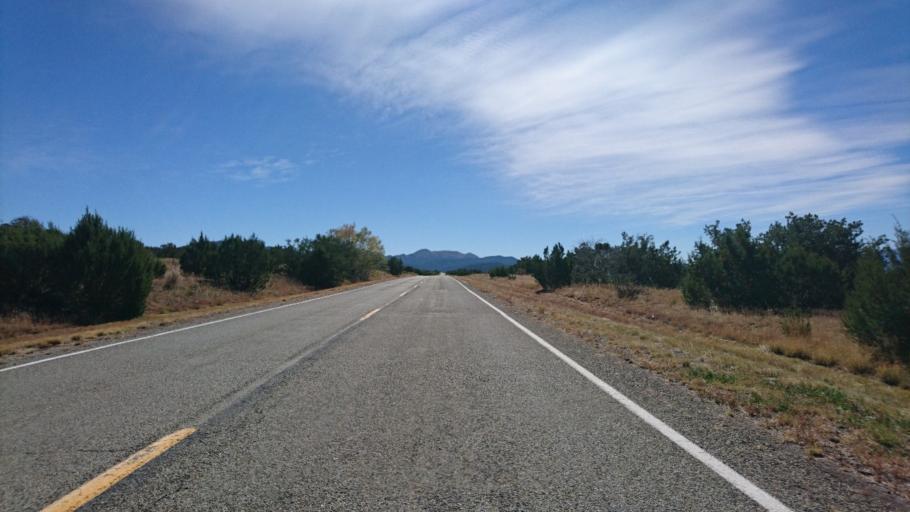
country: US
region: New Mexico
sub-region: Bernalillo County
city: Sandia Knolls
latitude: 35.3171
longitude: -106.2151
